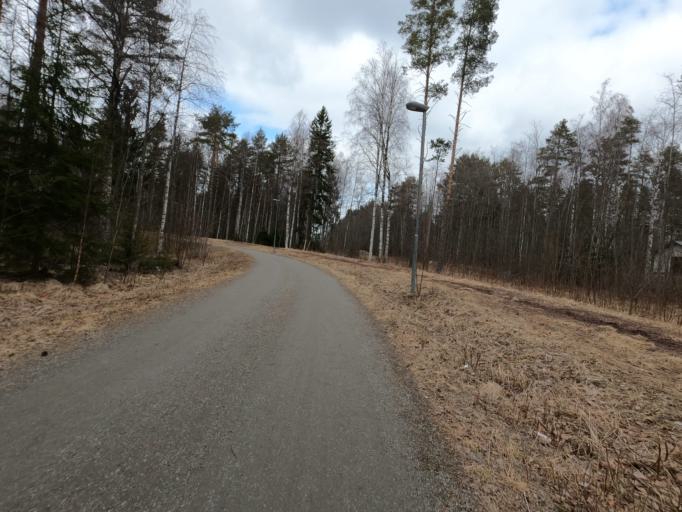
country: FI
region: North Karelia
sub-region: Joensuu
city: Joensuu
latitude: 62.5729
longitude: 29.8126
